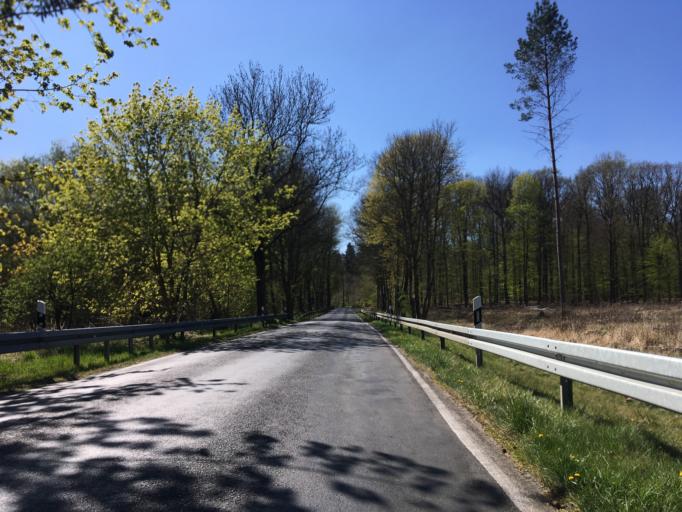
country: DE
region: Brandenburg
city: Bernau bei Berlin
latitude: 52.7282
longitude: 13.5668
